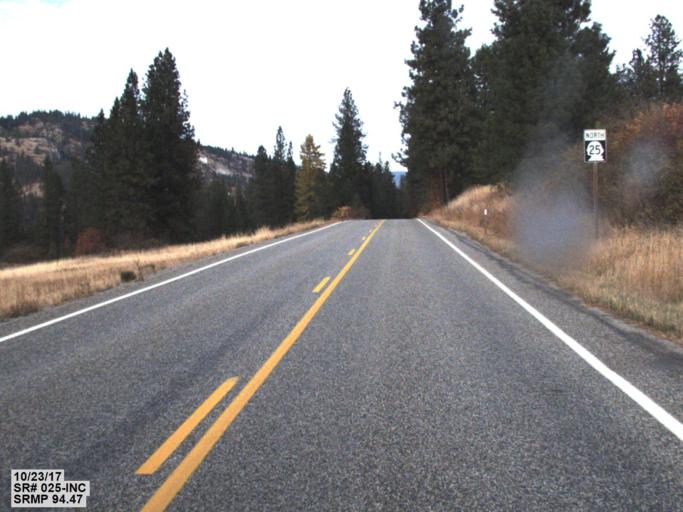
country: US
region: Washington
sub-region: Stevens County
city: Kettle Falls
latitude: 48.7535
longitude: -118.0433
